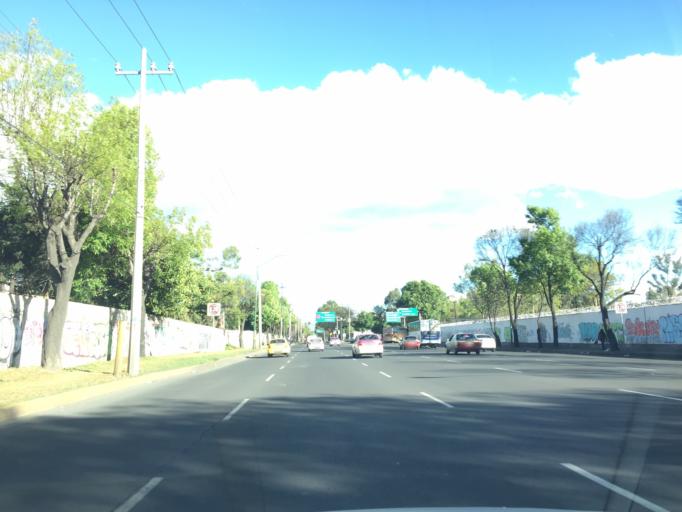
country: MX
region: Mexico
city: Colonia Lindavista
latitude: 19.4861
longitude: -99.1406
